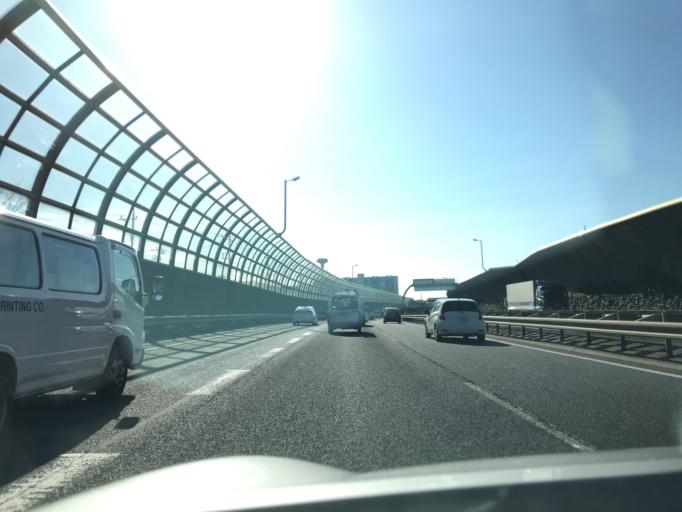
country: JP
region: Chiba
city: Chiba
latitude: 35.6570
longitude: 140.1052
